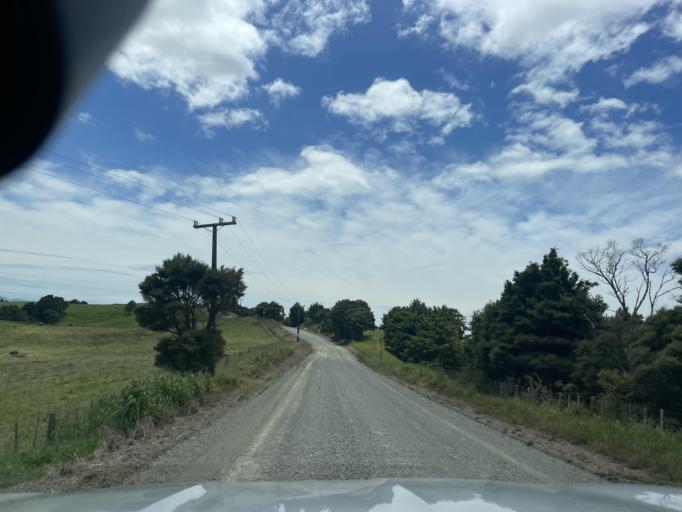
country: NZ
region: Auckland
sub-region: Auckland
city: Wellsford
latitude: -36.1612
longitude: 174.5336
